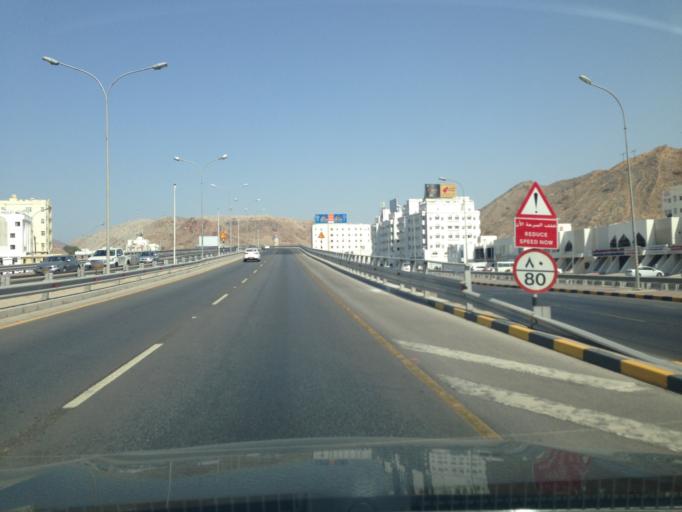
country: OM
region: Muhafazat Masqat
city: Muscat
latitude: 23.5874
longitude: 58.5357
